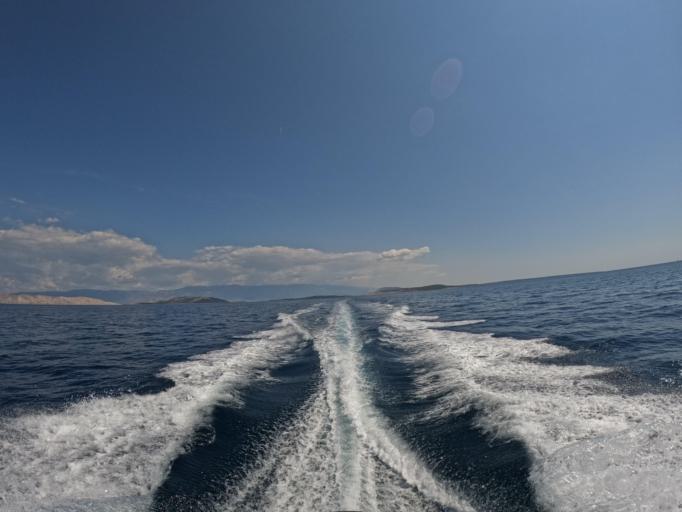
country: HR
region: Primorsko-Goranska
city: Lopar
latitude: 44.8823
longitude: 14.6483
